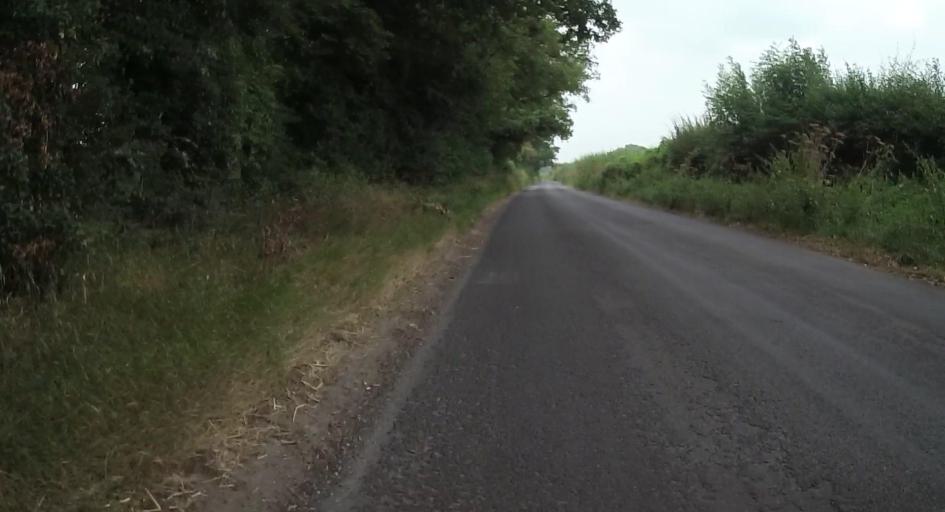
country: GB
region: England
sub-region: Hampshire
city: Old Basing
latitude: 51.2489
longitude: -1.0429
